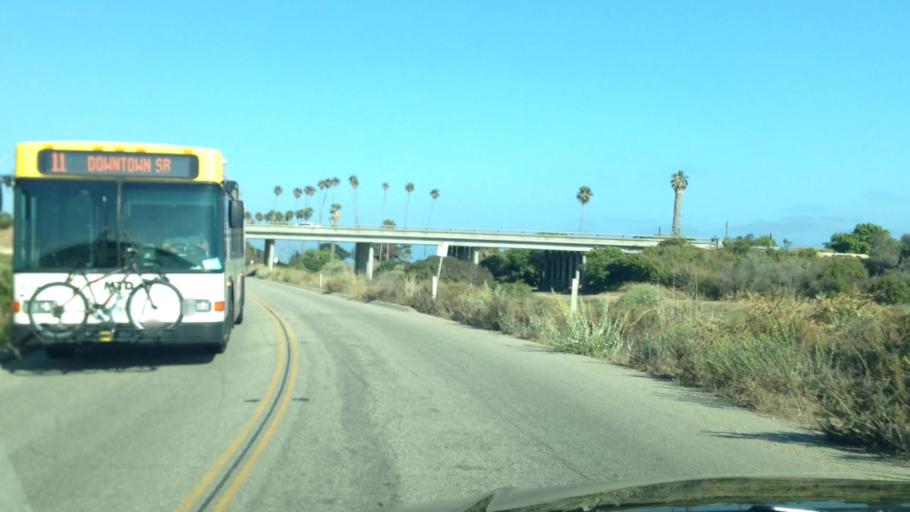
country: US
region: California
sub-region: Santa Barbara County
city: Goleta
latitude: 34.4186
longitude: -119.8348
